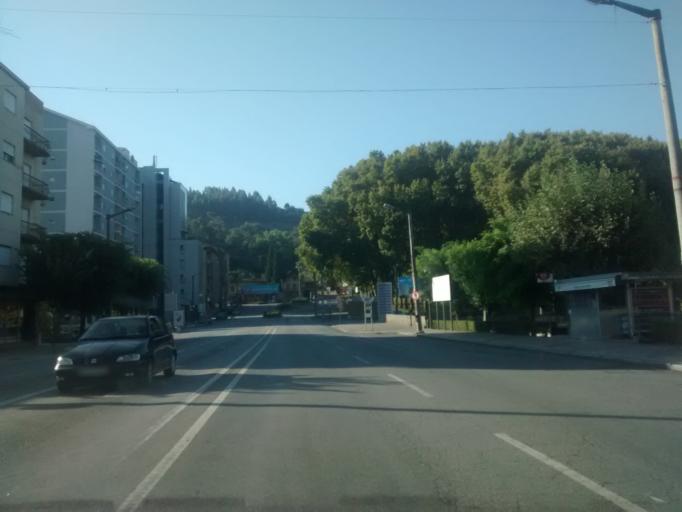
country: PT
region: Braga
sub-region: Braga
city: Braga
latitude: 41.5437
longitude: -8.4186
